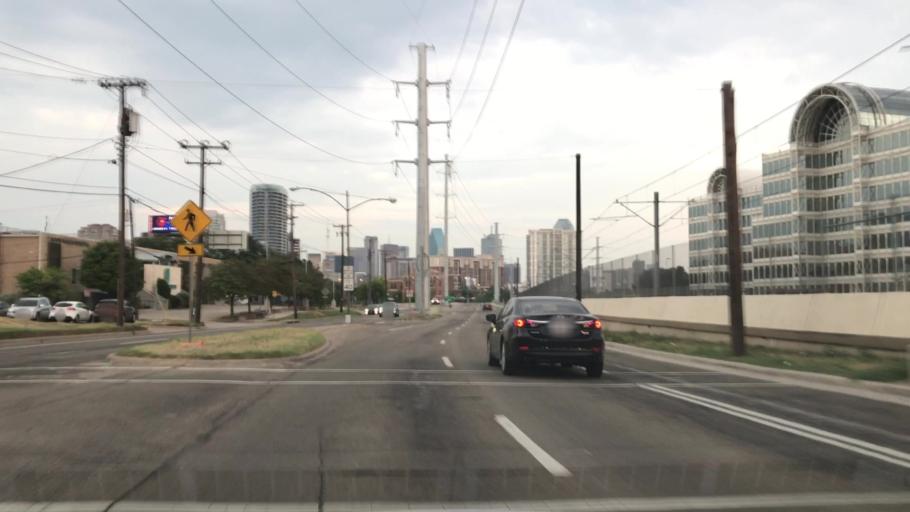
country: US
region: Texas
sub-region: Dallas County
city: Dallas
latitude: 32.8031
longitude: -96.8194
